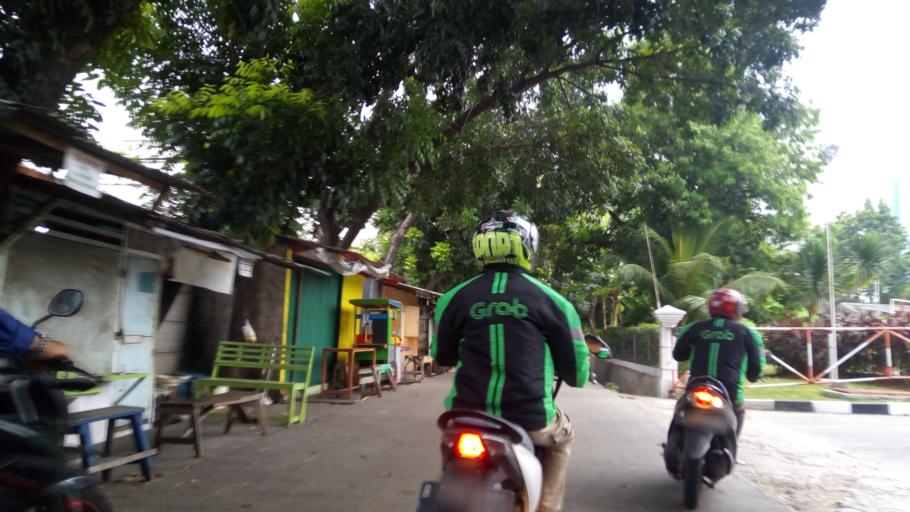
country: ID
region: Jakarta Raya
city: Jakarta
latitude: -6.1494
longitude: 106.8383
